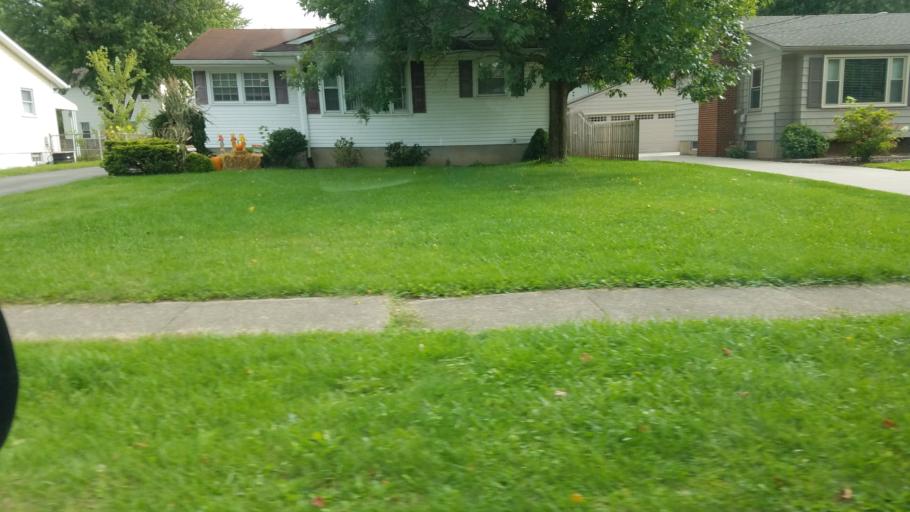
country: US
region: Ohio
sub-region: Mahoning County
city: Poland
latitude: 41.0371
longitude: -80.6253
